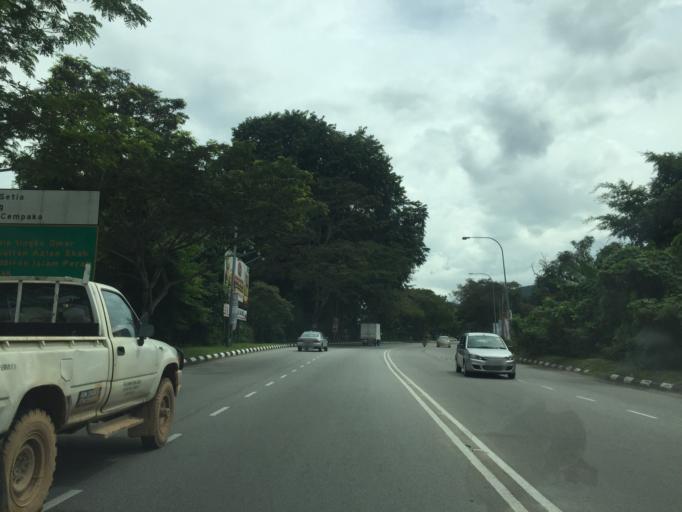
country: MY
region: Perak
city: Ipoh
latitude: 4.5689
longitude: 101.1147
